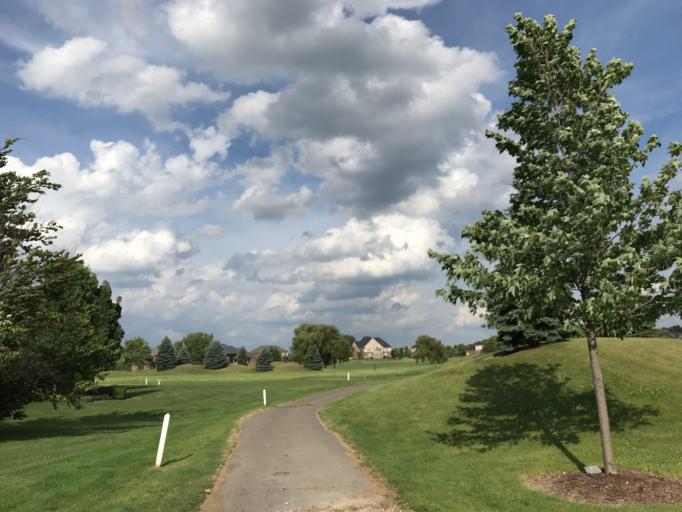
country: US
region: Michigan
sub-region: Oakland County
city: South Lyon
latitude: 42.4604
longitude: -83.5860
